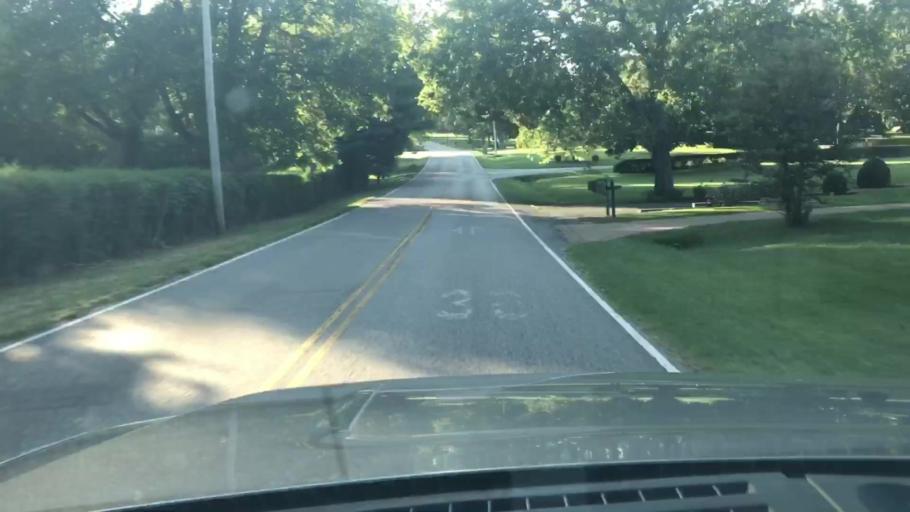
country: US
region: Tennessee
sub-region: Davidson County
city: Belle Meade
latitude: 36.1243
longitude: -86.8579
